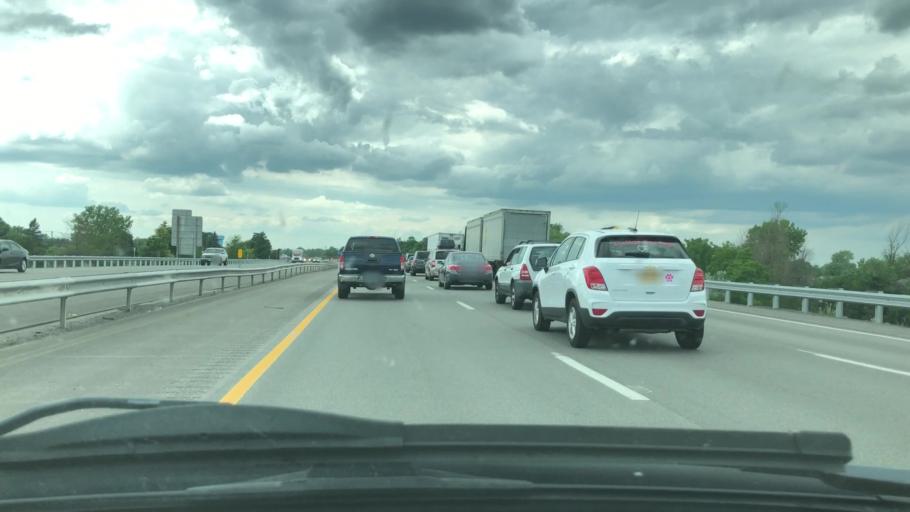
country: US
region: New York
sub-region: Erie County
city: Williamsville
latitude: 42.9516
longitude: -78.7398
